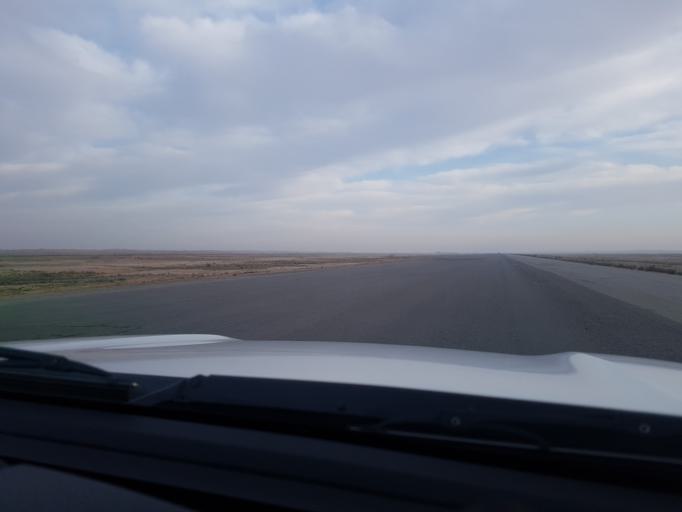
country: TM
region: Ahal
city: Abadan
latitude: 38.5060
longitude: 58.5067
